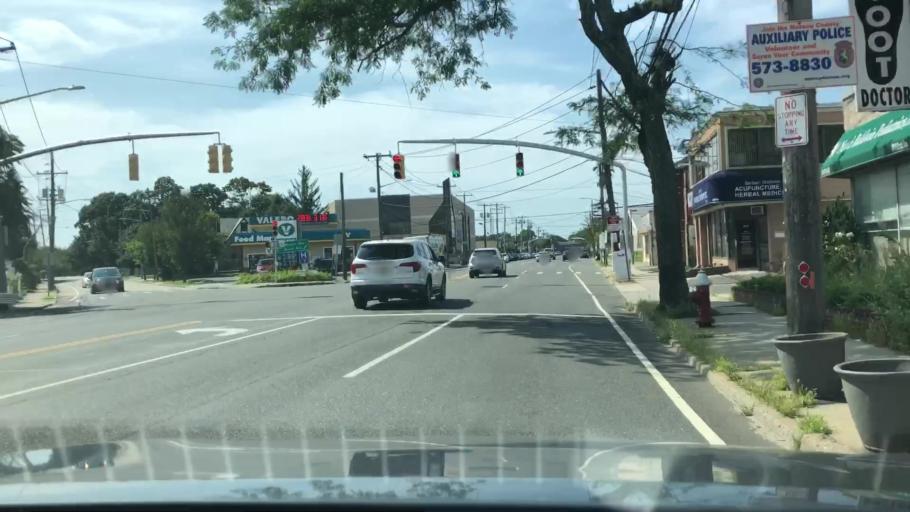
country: US
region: New York
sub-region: Nassau County
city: Baldwin
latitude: 40.6613
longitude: -73.6078
